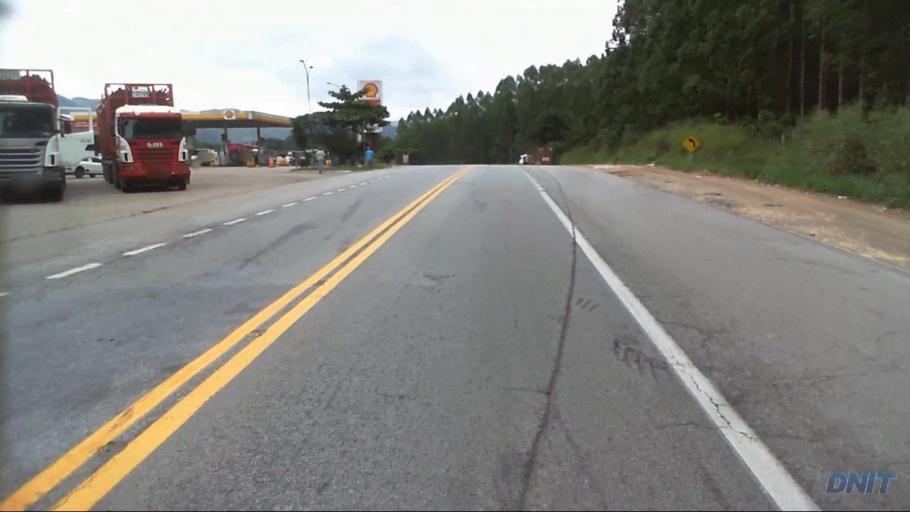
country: BR
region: Minas Gerais
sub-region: Barao De Cocais
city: Barao de Cocais
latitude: -19.7480
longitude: -43.4923
